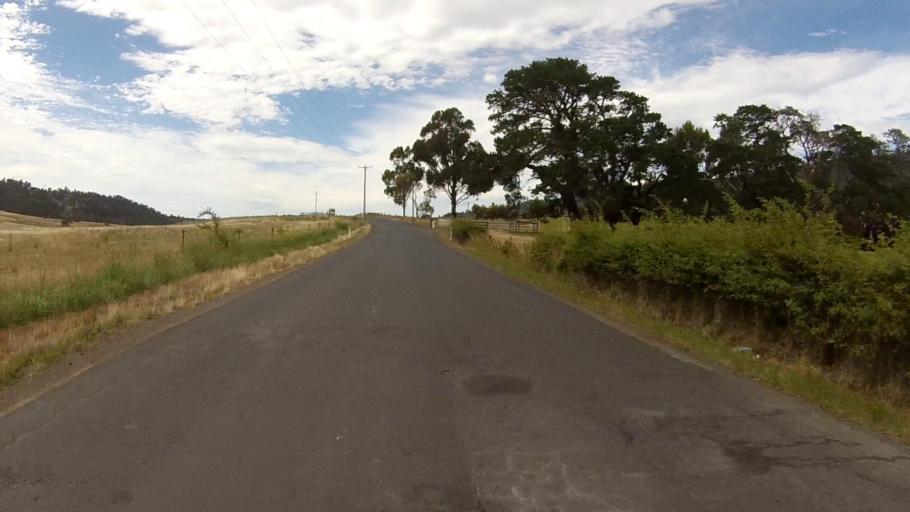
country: AU
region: Tasmania
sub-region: Brighton
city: Old Beach
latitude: -42.7267
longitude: 147.3439
